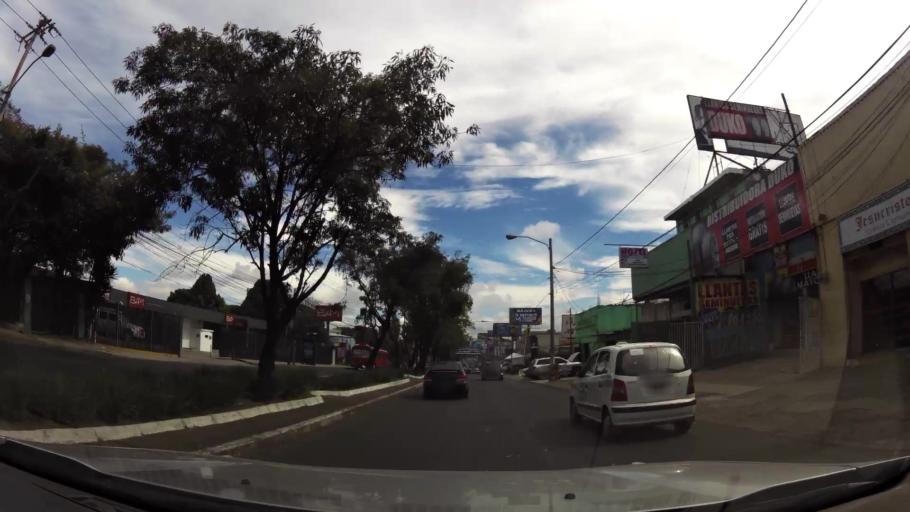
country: GT
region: Guatemala
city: Mixco
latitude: 14.6418
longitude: -90.5702
